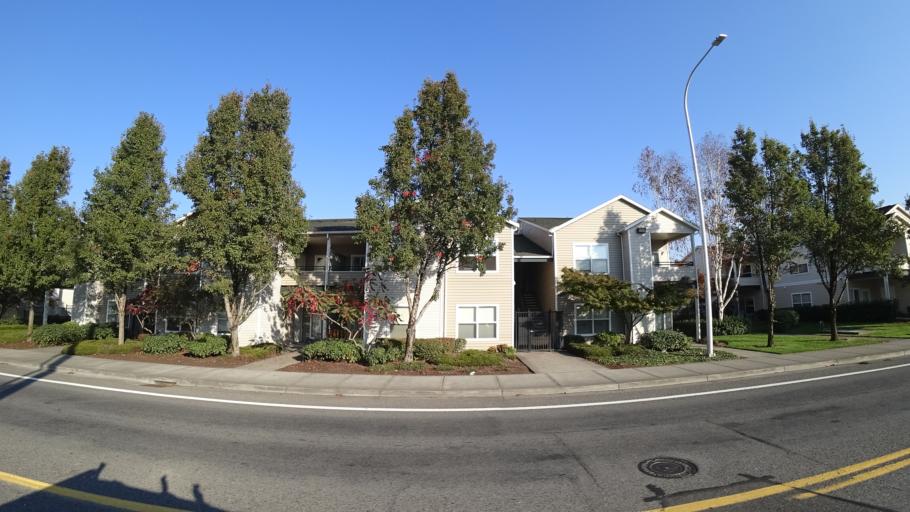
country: US
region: Oregon
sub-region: Multnomah County
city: Gresham
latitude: 45.5160
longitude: -122.4552
